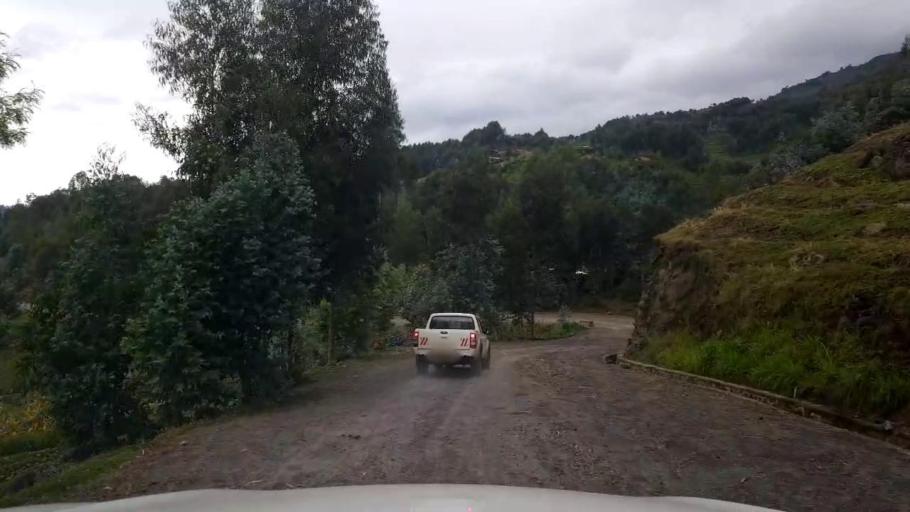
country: RW
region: Northern Province
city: Musanze
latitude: -1.4977
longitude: 29.5344
